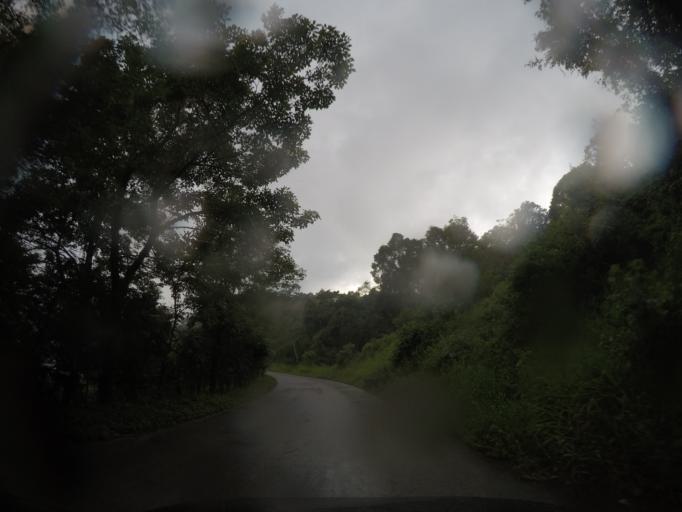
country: MX
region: Oaxaca
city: San Gabriel Mixtepec
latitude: 16.1113
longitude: -97.0672
